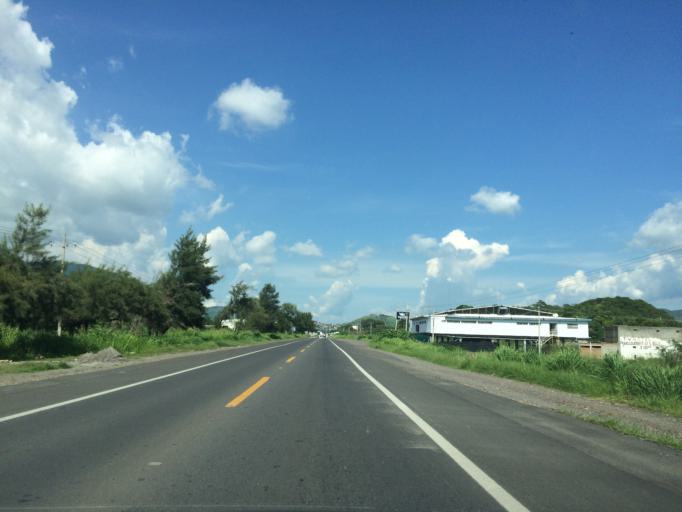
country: MX
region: Nayarit
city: Ixtlan del Rio
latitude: 21.0370
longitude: -104.3960
